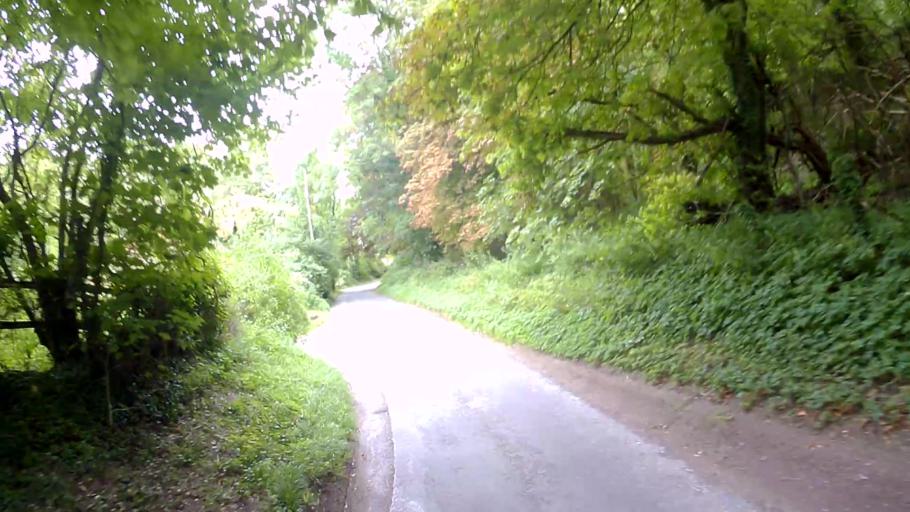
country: GB
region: England
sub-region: Hampshire
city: Kings Worthy
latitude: 51.1685
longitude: -1.3533
